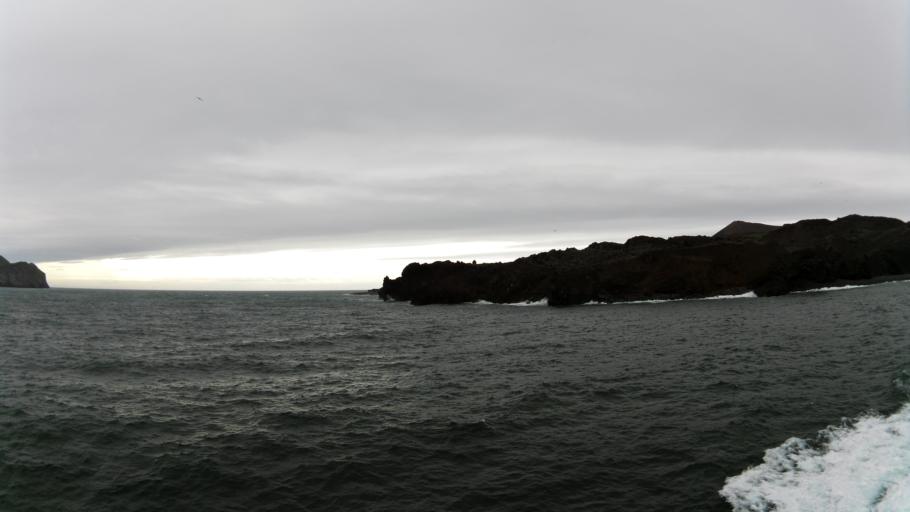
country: IS
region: South
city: Vestmannaeyjar
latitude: 63.4479
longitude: -20.2428
